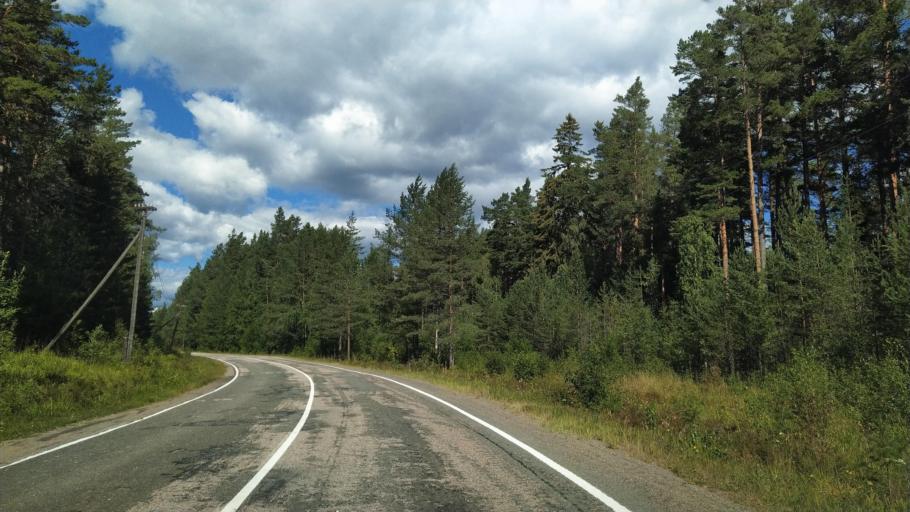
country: RU
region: Leningrad
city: Priozersk
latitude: 60.9878
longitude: 30.2636
